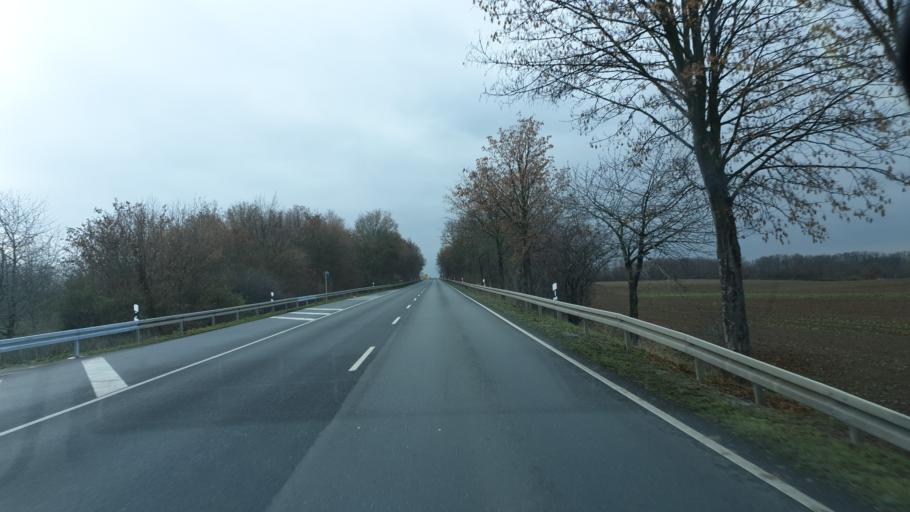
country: DE
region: Saxony-Anhalt
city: Stossen
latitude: 51.1191
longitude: 11.9091
